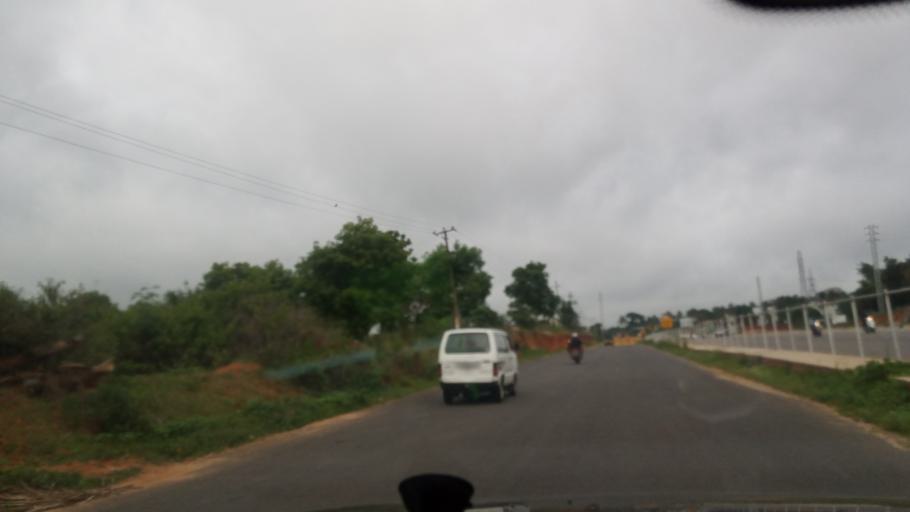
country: IN
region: Karnataka
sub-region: Ramanagara
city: Ramanagaram
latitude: 12.7692
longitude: 77.3409
